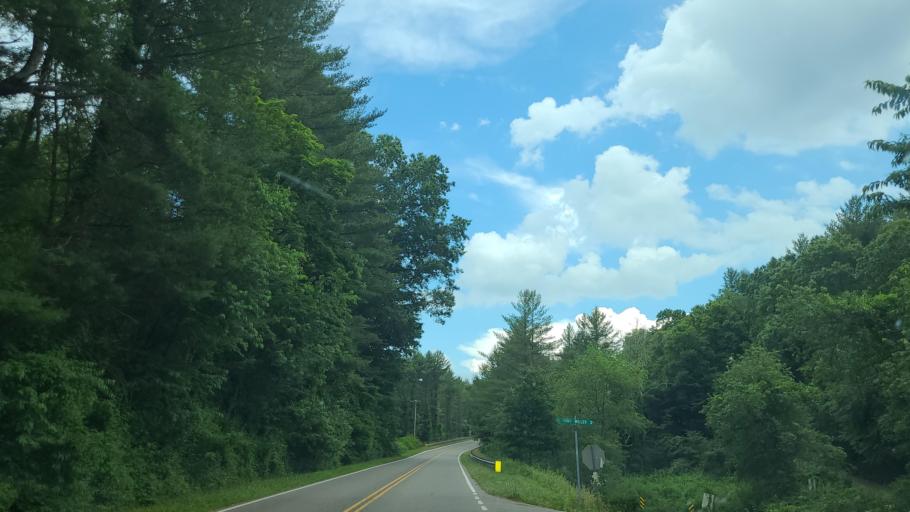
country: US
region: North Carolina
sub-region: Alleghany County
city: Sparta
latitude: 36.4098
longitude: -81.2638
